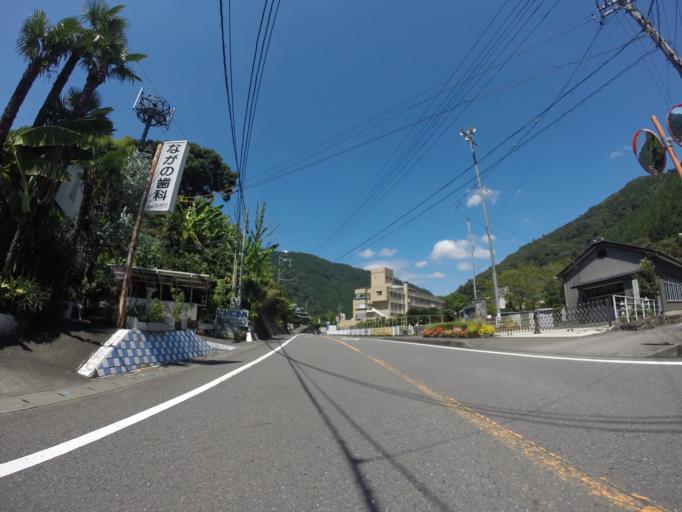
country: JP
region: Shizuoka
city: Shizuoka-shi
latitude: 35.0219
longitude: 138.2569
